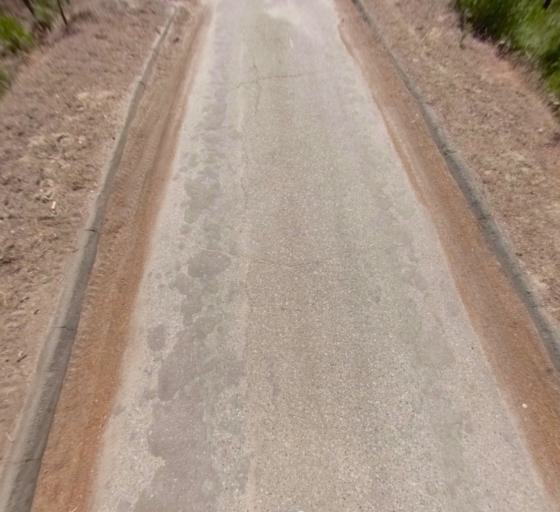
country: US
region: California
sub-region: Madera County
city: Oakhurst
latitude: 37.4116
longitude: -119.3478
